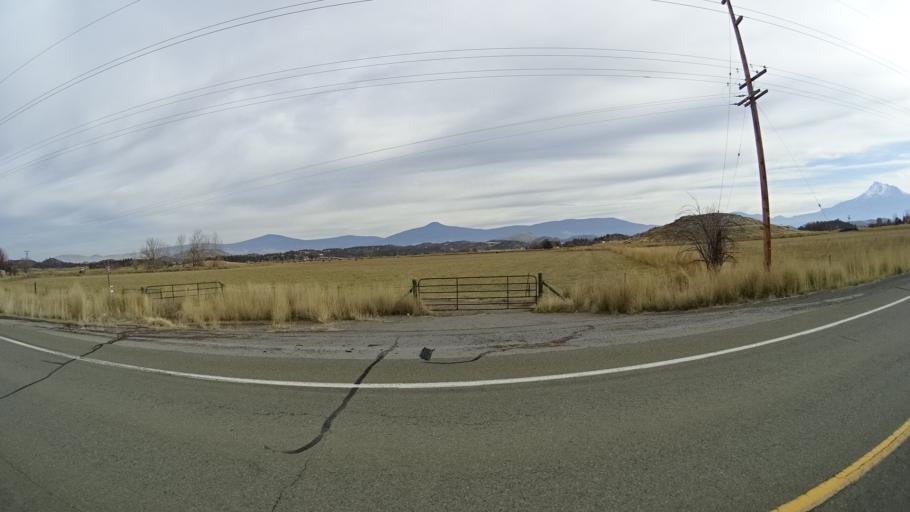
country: US
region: California
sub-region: Siskiyou County
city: Montague
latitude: 41.6601
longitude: -122.5200
